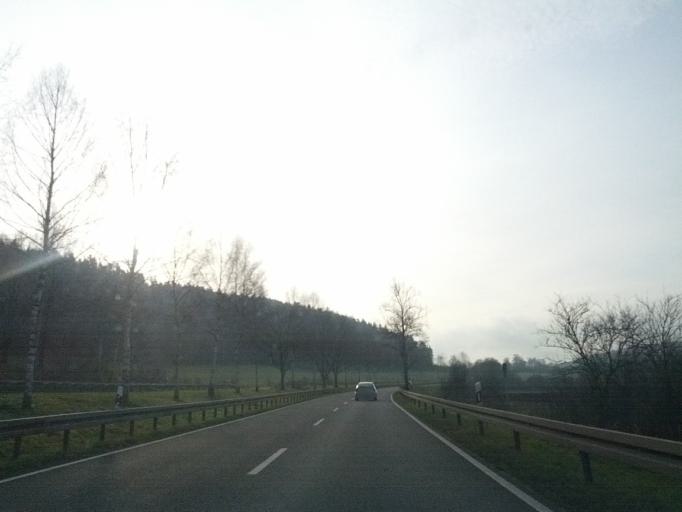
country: DE
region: Thuringia
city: Wallbach
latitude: 50.6402
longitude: 10.3811
